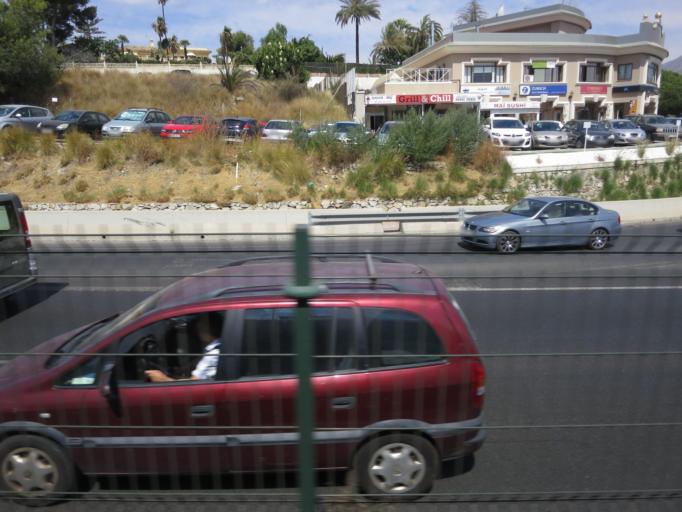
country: ES
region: Andalusia
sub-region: Provincia de Malaga
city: Marbella
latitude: 36.4888
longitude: -4.9576
